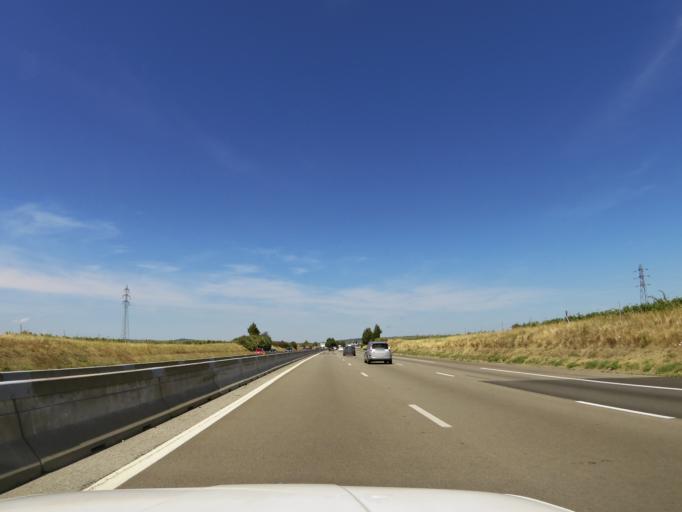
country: FR
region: Rhone-Alpes
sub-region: Departement de la Drome
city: La Roche-de-Glun
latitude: 45.0310
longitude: 4.8754
